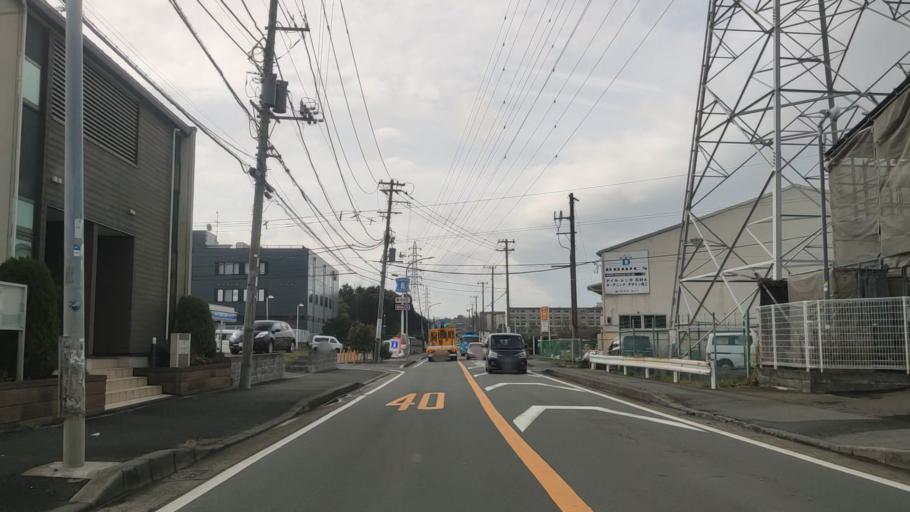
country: JP
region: Kanagawa
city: Fujisawa
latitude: 35.3780
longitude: 139.5257
